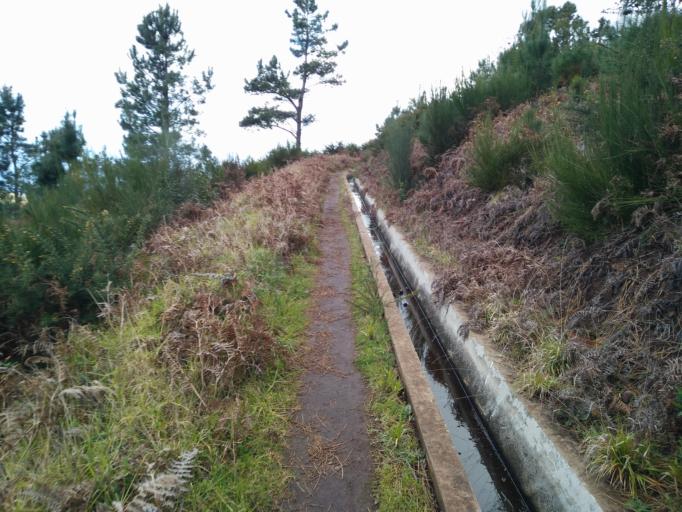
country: PT
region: Madeira
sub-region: Calheta
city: Faja da Ovelha
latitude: 32.8175
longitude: -17.2292
